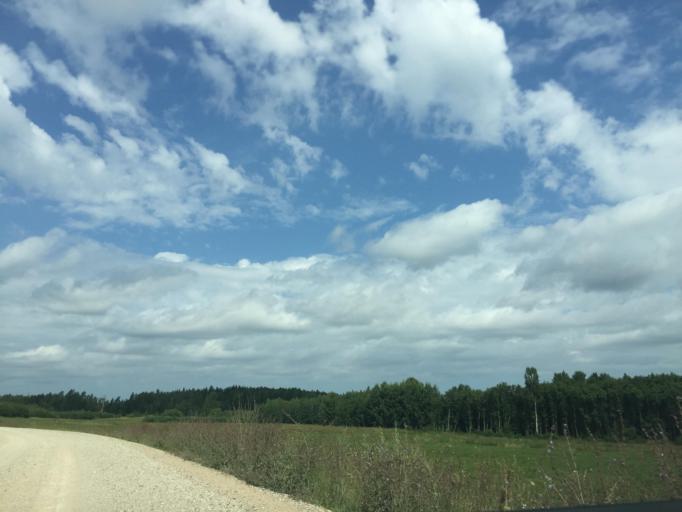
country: LV
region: Kandava
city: Kandava
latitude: 57.0031
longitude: 22.8547
